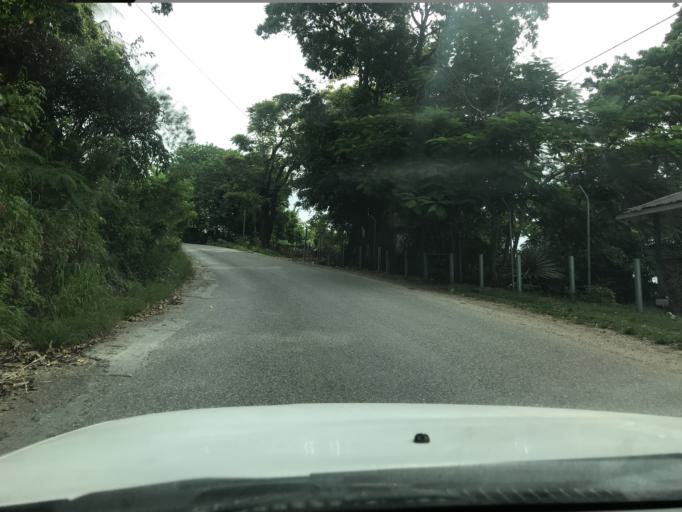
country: SB
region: Guadalcanal
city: Honiara
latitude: -9.4321
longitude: 159.9454
